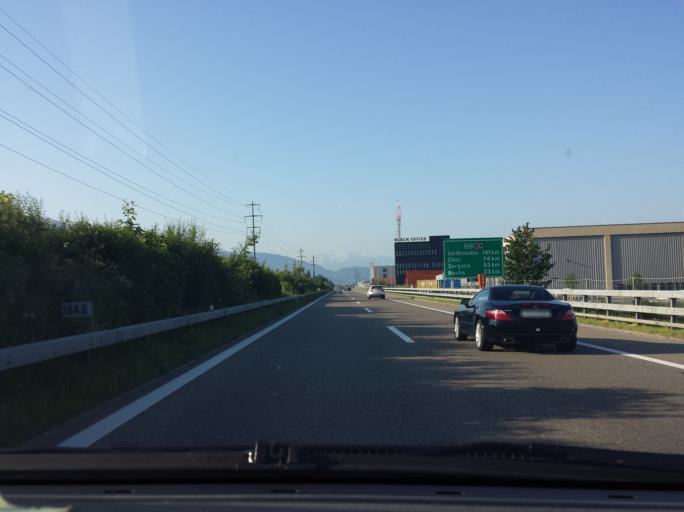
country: AT
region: Vorarlberg
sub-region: Politischer Bezirk Dornbirn
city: Lustenau
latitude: 47.4167
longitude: 9.6472
